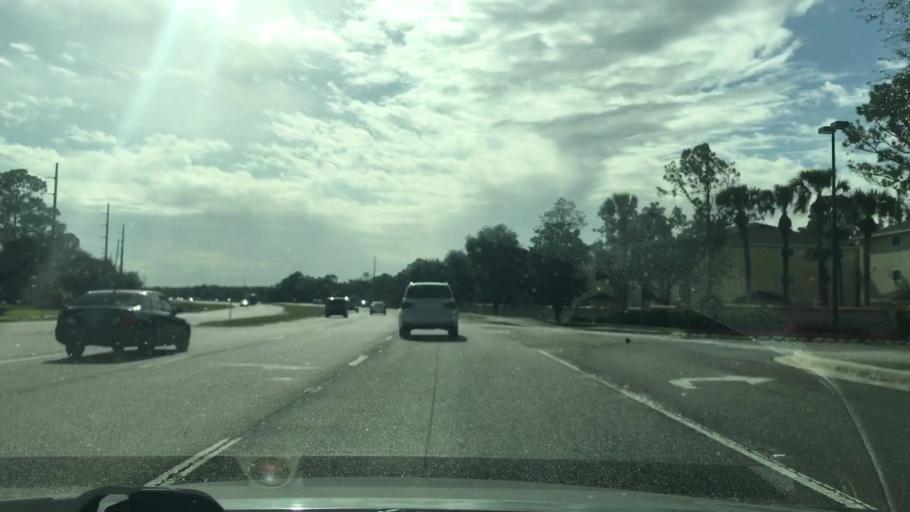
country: US
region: Florida
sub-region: Osceola County
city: Celebration
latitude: 28.3641
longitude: -81.5020
